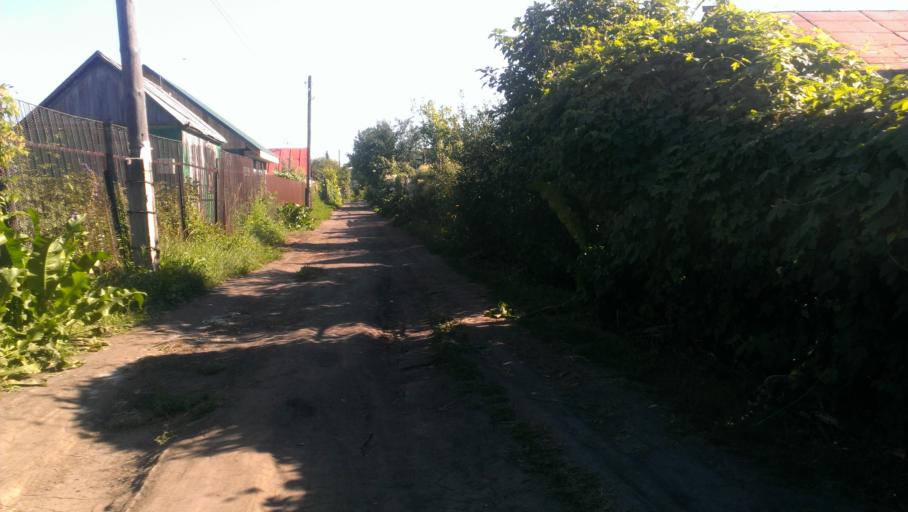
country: RU
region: Altai Krai
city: Novosilikatnyy
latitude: 53.3232
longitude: 83.6694
